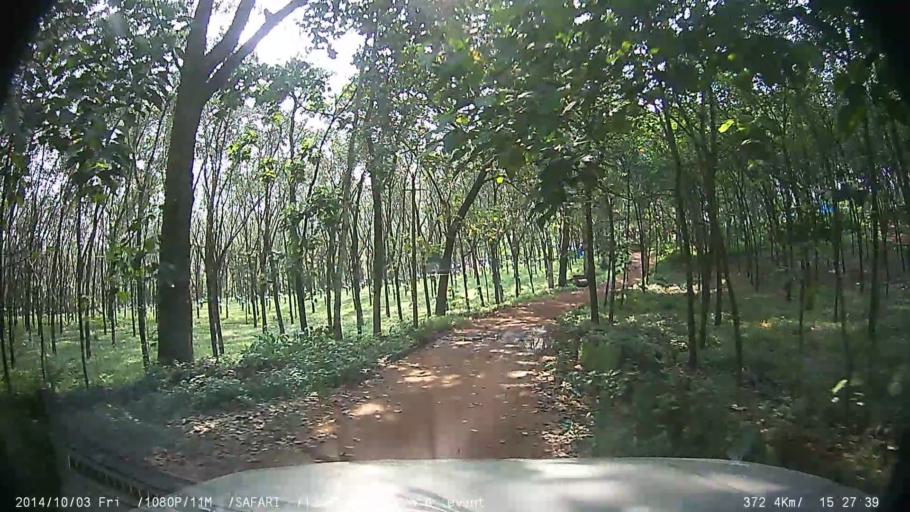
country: IN
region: Kerala
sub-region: Ernakulam
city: Muvattupuzha
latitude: 9.9292
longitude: 76.5694
